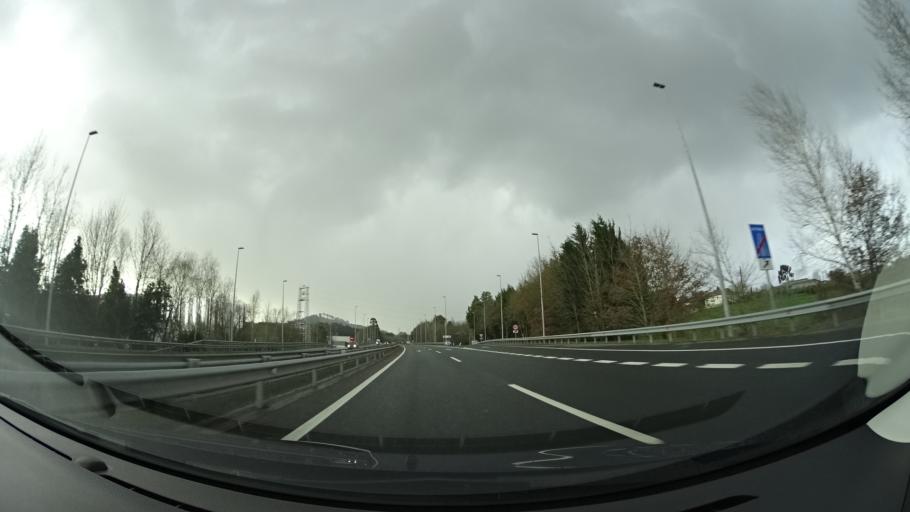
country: ES
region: Basque Country
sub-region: Bizkaia
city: Gatika
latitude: 43.3423
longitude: -2.8633
